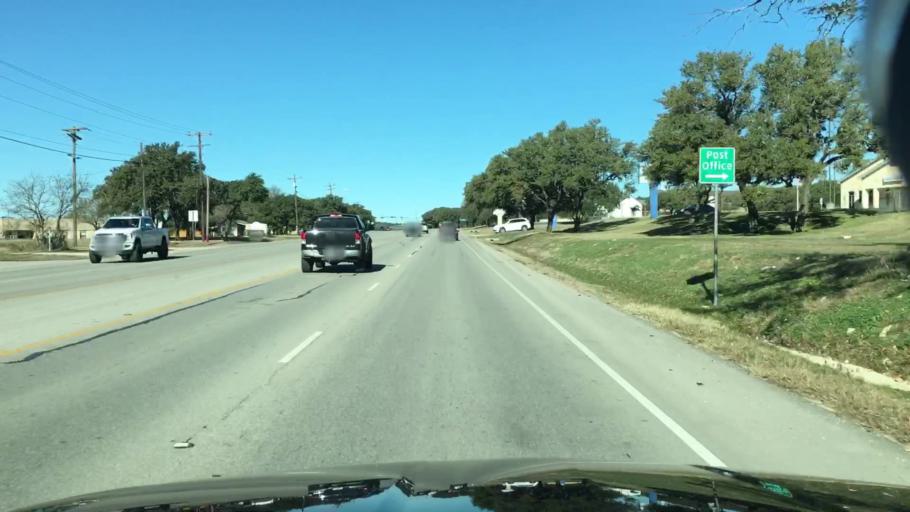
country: US
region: Texas
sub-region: Hays County
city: Dripping Springs
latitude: 30.1992
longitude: -98.1080
